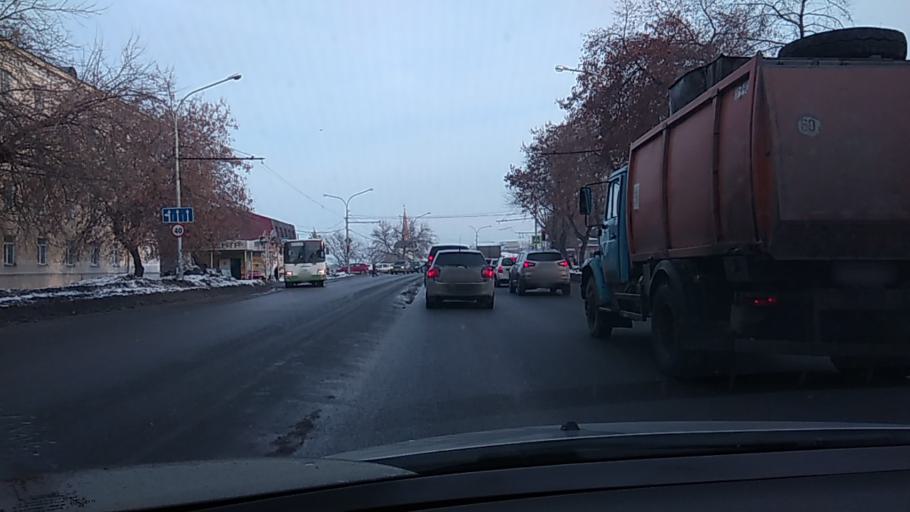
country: RU
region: Sverdlovsk
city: Kamensk-Ural'skiy
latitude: 56.3932
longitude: 61.9521
